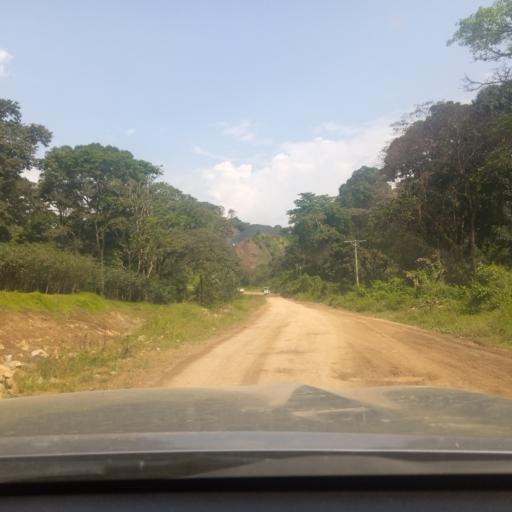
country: ET
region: Southern Nations, Nationalities, and People's Region
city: Tippi
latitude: 7.0703
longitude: 35.4362
